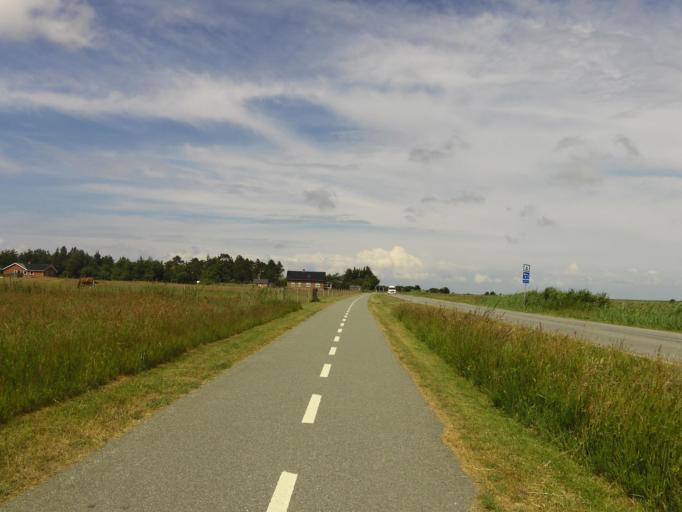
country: DE
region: Schleswig-Holstein
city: List
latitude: 55.1598
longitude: 8.5519
